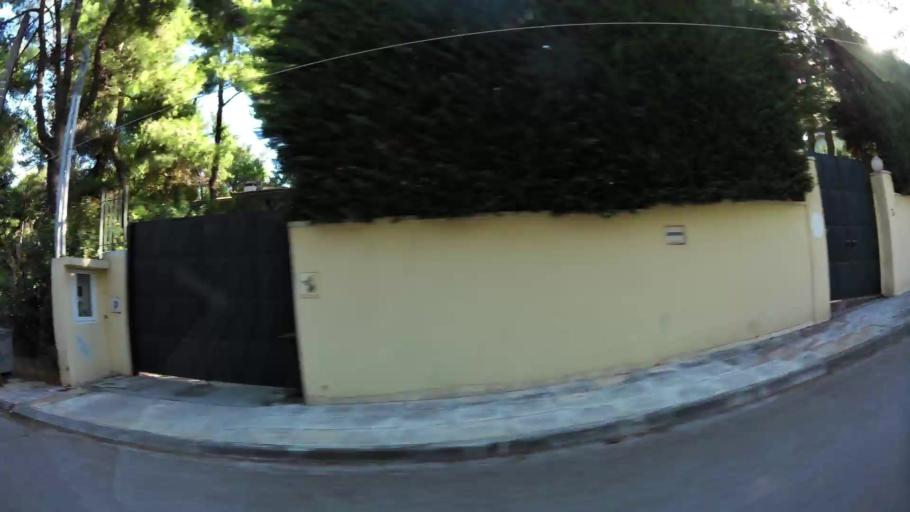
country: GR
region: Attica
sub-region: Nomarchia Anatolikis Attikis
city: Stamata
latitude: 38.1338
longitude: 23.8774
